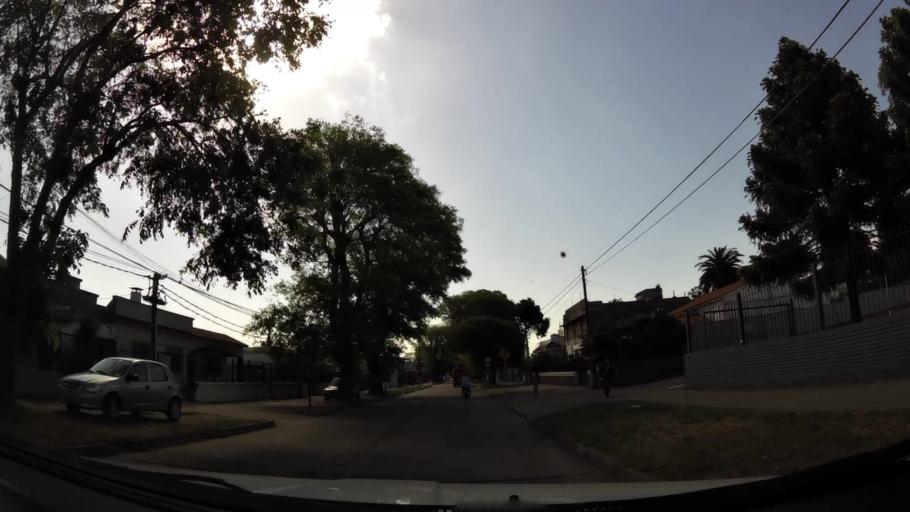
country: UY
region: Montevideo
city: Montevideo
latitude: -34.8362
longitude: -56.2121
